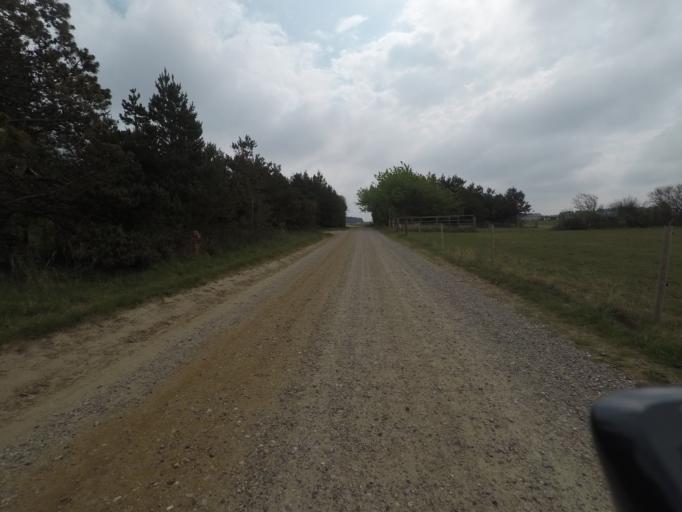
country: DE
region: Schleswig-Holstein
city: List
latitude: 55.0878
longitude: 8.5245
